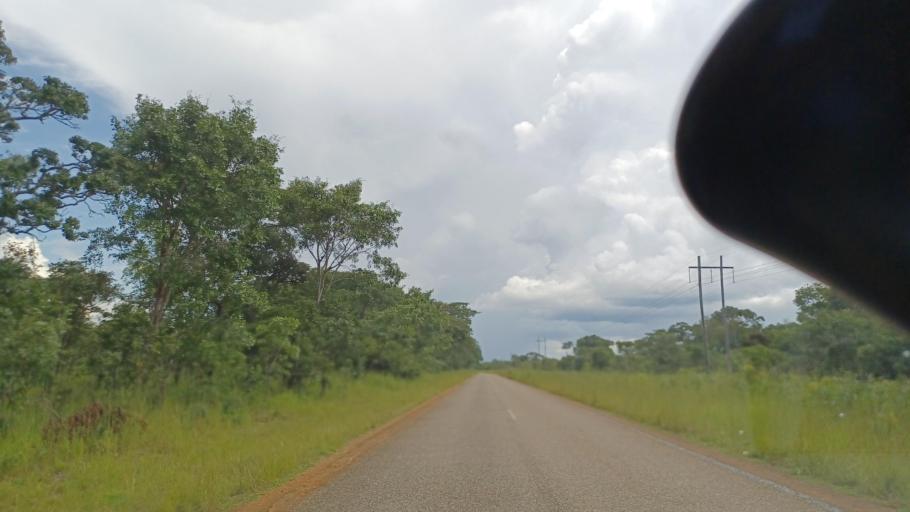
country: ZM
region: North-Western
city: Kasempa
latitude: -13.1486
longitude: 25.8776
